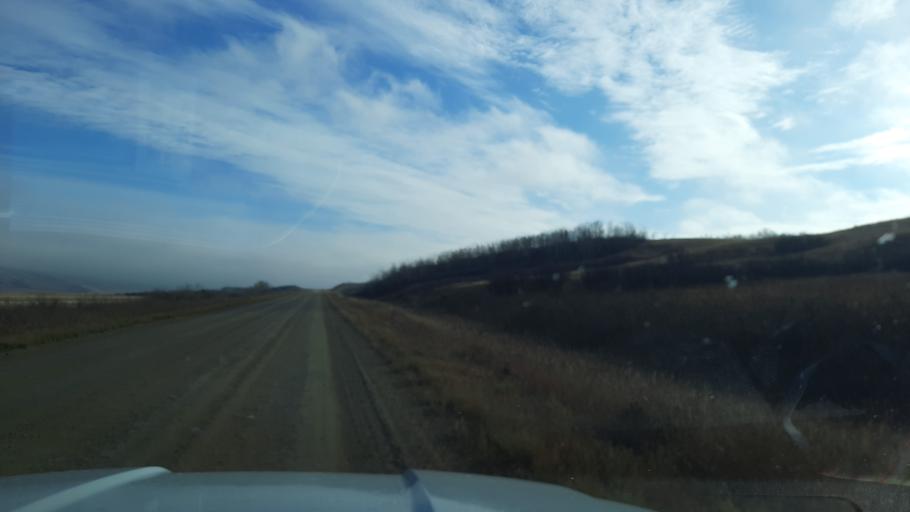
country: CA
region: Saskatchewan
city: Pilot Butte
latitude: 50.7838
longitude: -104.2361
